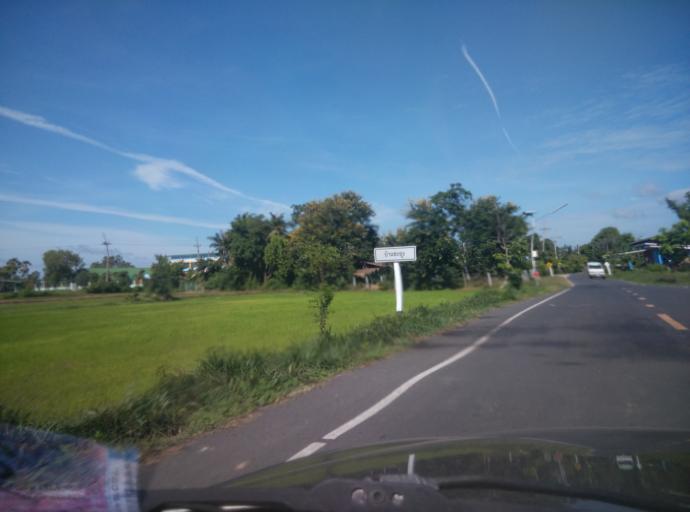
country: TH
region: Sisaket
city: Uthumphon Phisai
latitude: 15.1199
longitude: 104.2265
